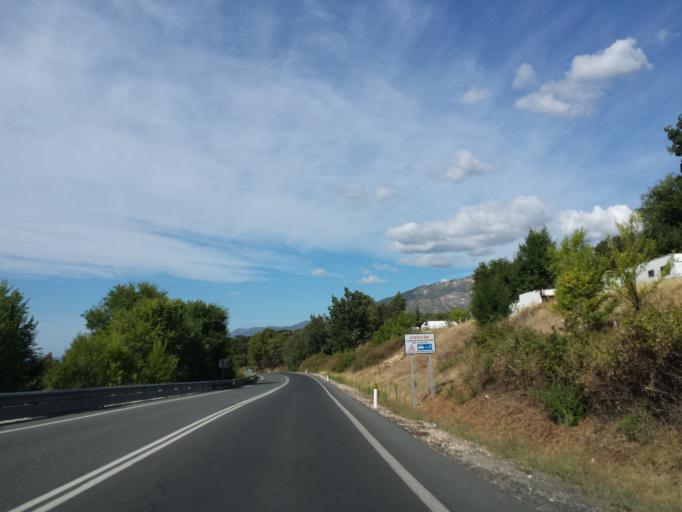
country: ES
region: Castille and Leon
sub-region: Provincia de Avila
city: Piedralaves
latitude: 40.3108
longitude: -4.7072
